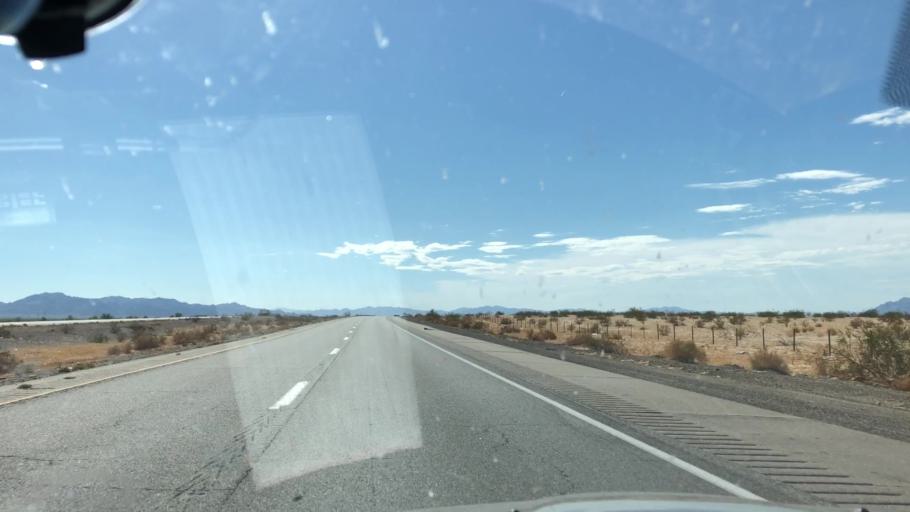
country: US
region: California
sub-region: Riverside County
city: Mesa Verde
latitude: 33.6439
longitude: -115.1121
